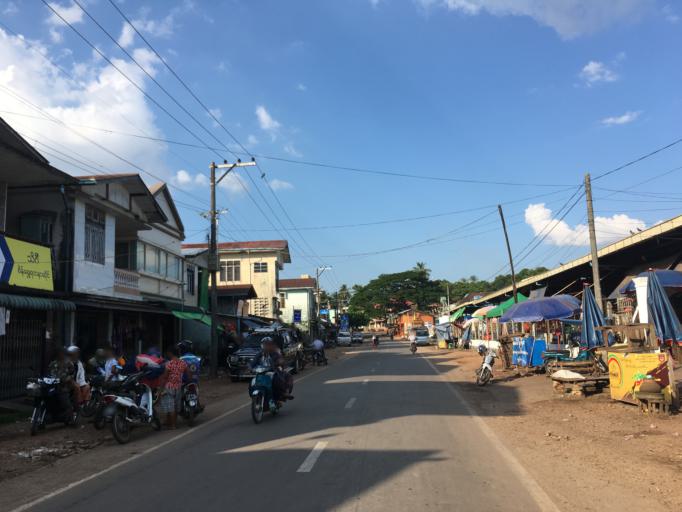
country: MM
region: Mon
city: Mawlamyine
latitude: 16.4557
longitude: 97.6262
